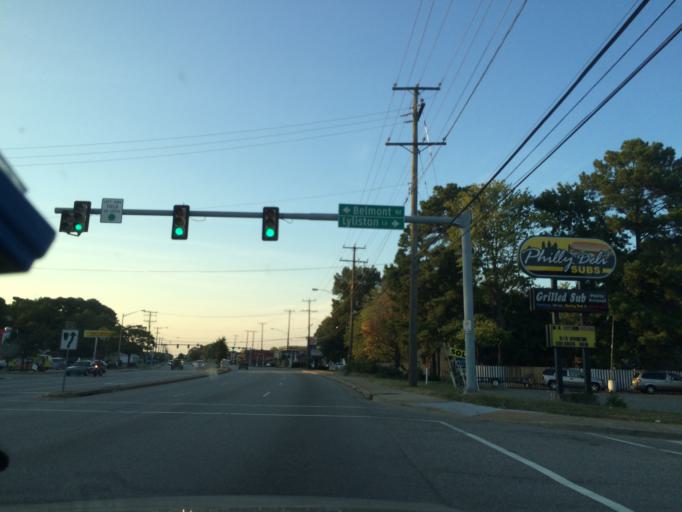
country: US
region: Virginia
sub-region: City of Newport News
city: Newport News
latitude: 37.0500
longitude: -76.4603
